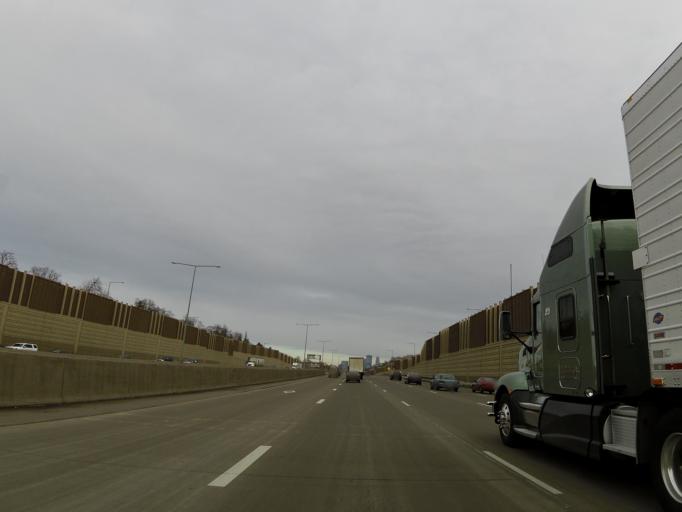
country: US
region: Minnesota
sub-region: Hennepin County
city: Richfield
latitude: 44.9205
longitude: -93.2747
